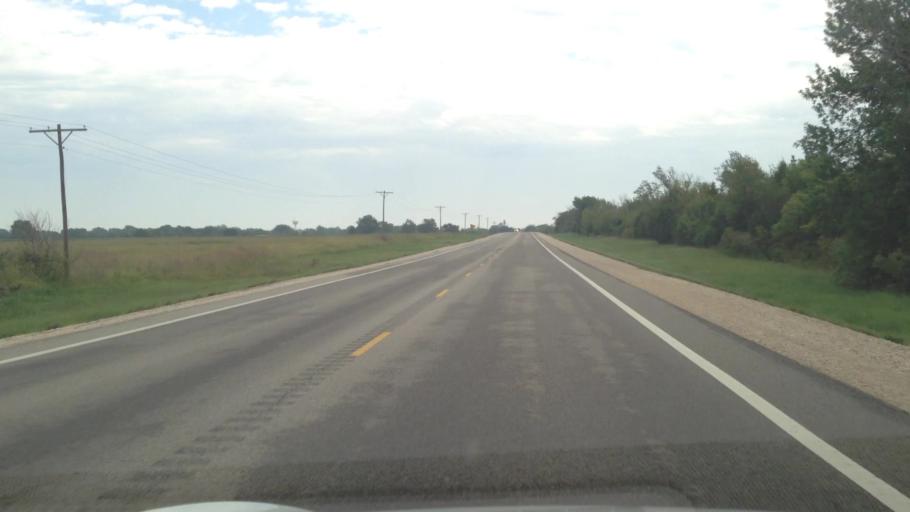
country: US
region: Kansas
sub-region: Allen County
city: Iola
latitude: 37.9024
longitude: -95.0874
